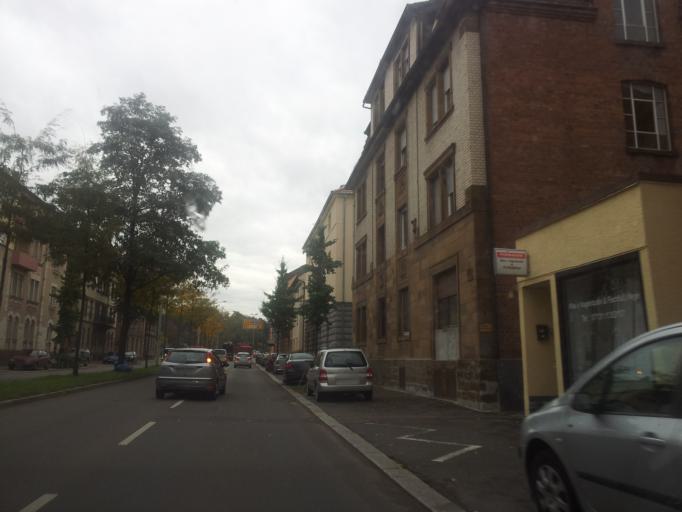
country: DE
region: Baden-Wuerttemberg
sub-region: Regierungsbezirk Stuttgart
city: Heilbronn
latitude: 49.1340
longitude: 9.2249
